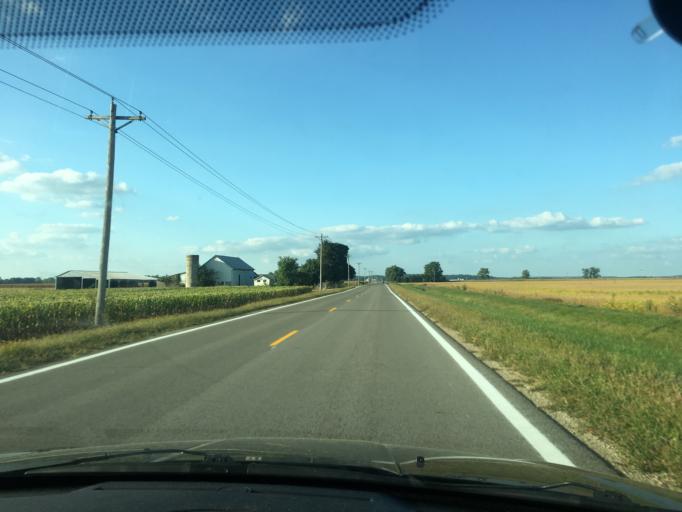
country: US
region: Ohio
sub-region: Logan County
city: West Liberty
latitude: 40.1883
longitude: -83.7817
